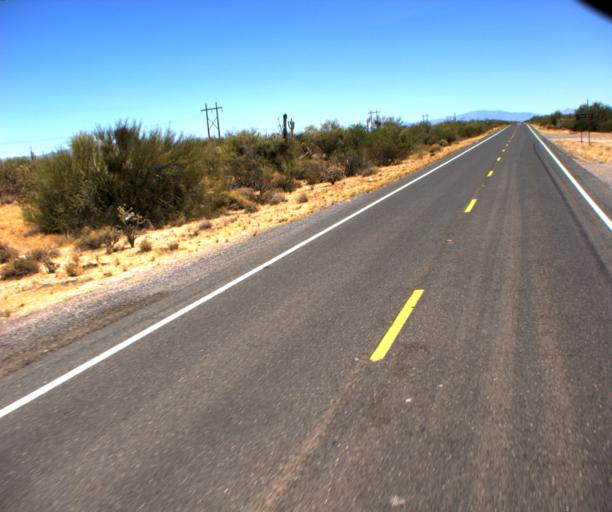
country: US
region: Arizona
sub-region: Pinal County
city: Florence
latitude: 32.8221
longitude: -111.2036
